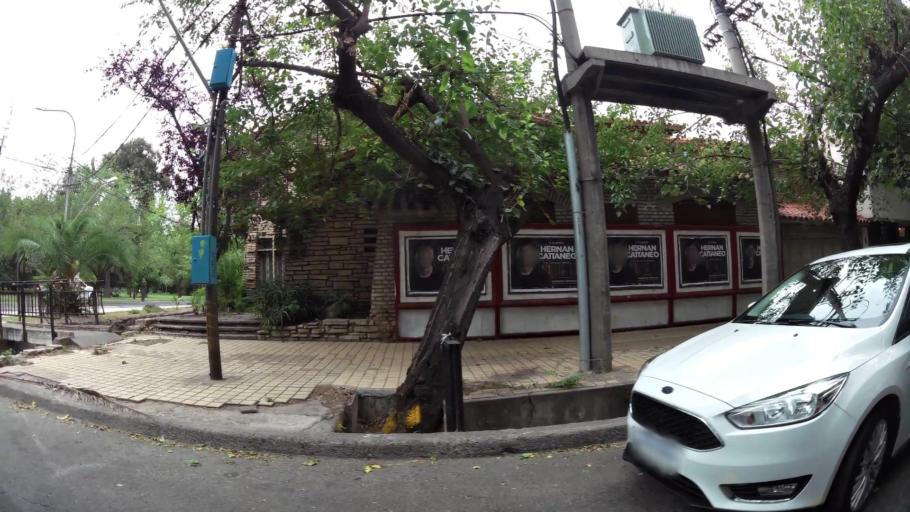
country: AR
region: Mendoza
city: Mendoza
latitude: -32.9024
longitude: -68.8527
